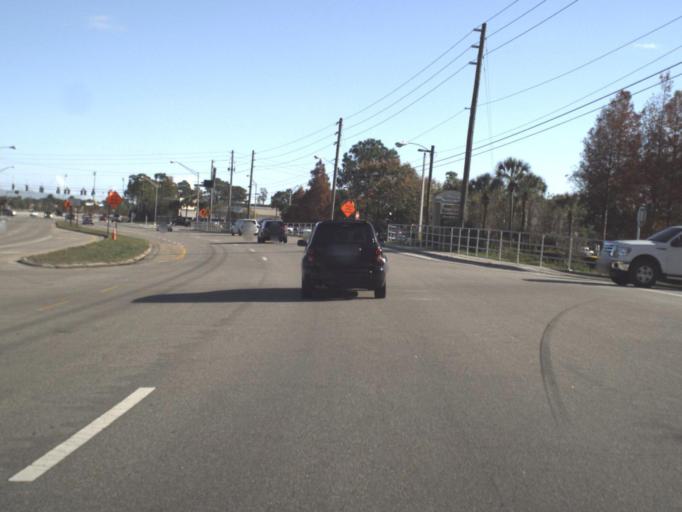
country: US
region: Florida
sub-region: Volusia County
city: Daytona Beach
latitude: 29.1831
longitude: -81.0809
